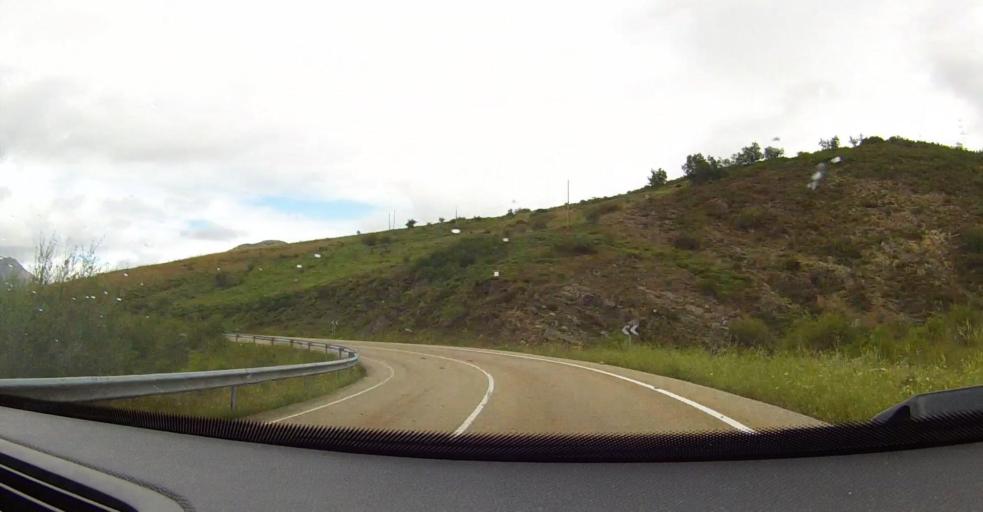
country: ES
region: Castille and Leon
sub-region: Provincia de Leon
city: Puebla de Lillo
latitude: 42.9363
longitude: -5.2709
